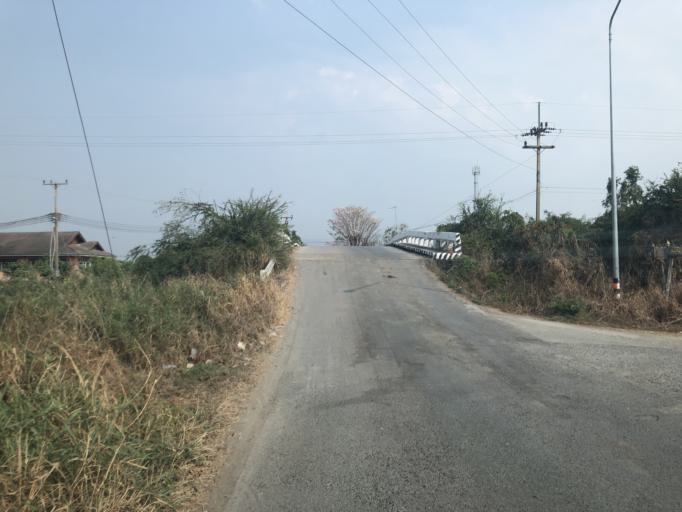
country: TH
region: Chachoengsao
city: Bang Pakong
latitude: 13.5117
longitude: 100.9258
